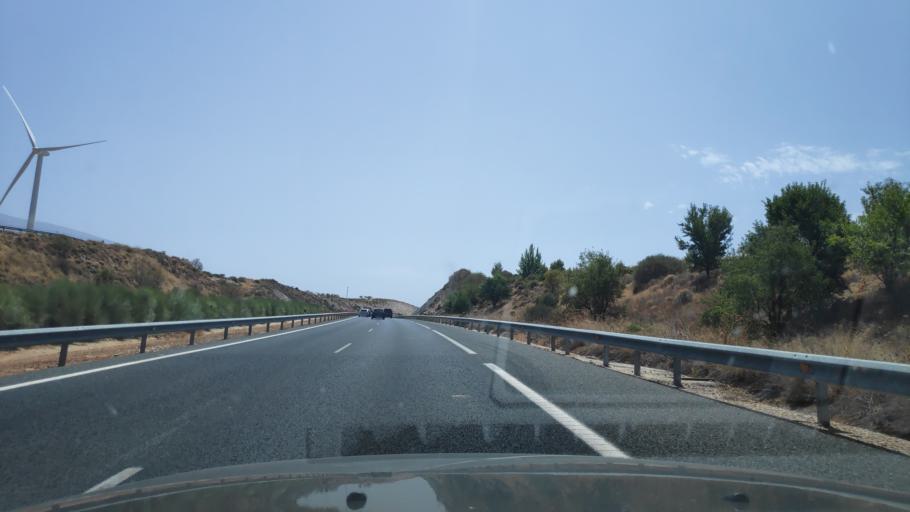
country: ES
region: Andalusia
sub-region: Provincia de Granada
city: Padul
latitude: 37.0045
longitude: -3.6364
